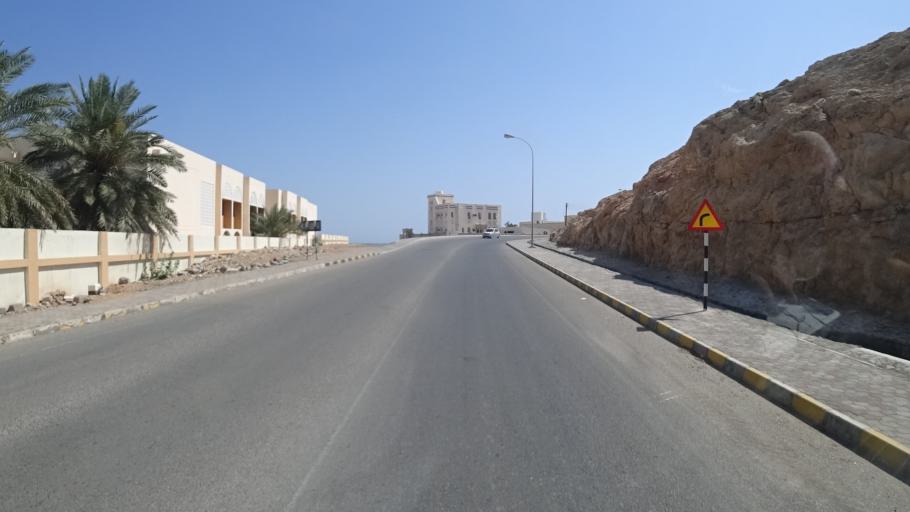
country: OM
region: Ash Sharqiyah
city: Sur
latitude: 22.5664
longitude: 59.5481
